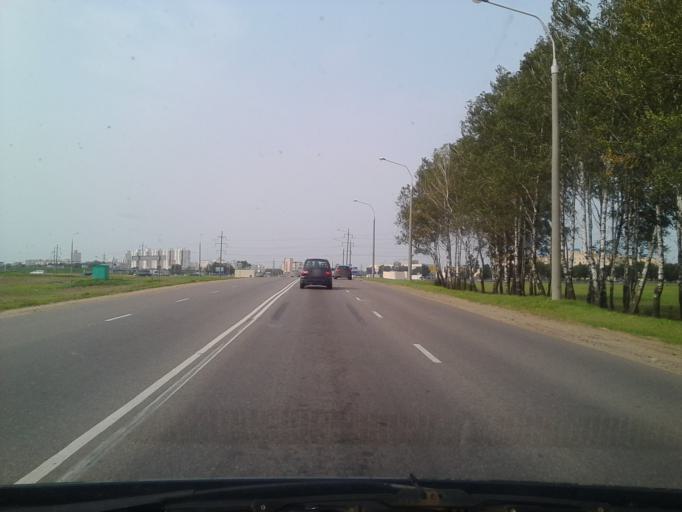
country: BY
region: Minsk
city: Hatava
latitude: 53.8305
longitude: 27.6138
